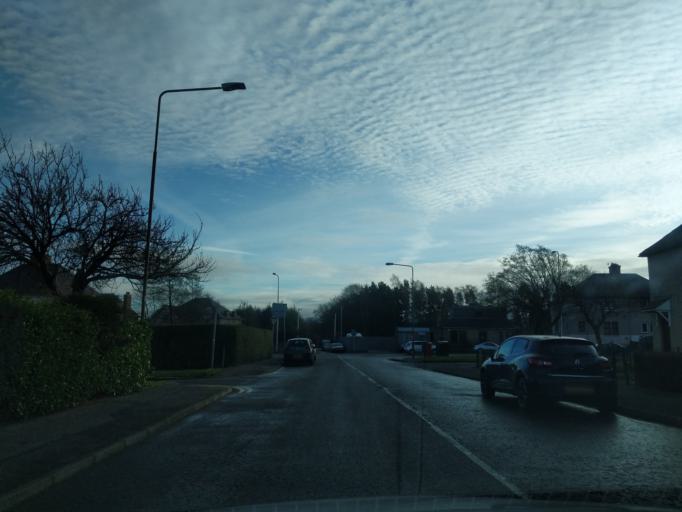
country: GB
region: Scotland
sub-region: Midlothian
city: Loanhead
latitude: 55.8762
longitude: -3.1629
